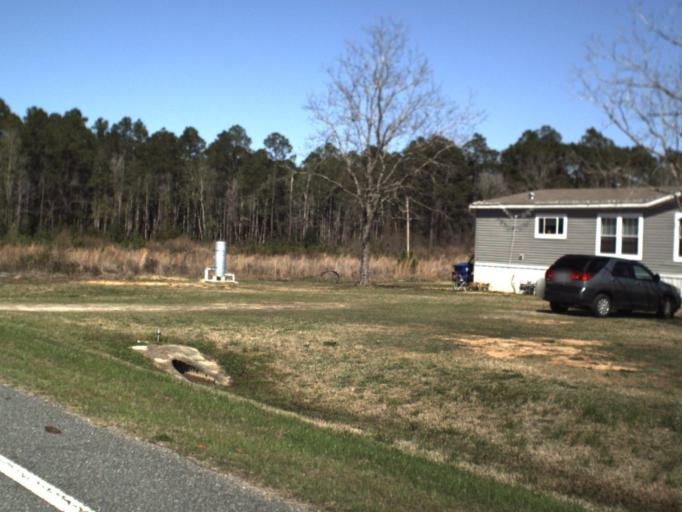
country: US
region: Florida
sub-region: Calhoun County
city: Blountstown
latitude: 30.3900
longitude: -85.0851
